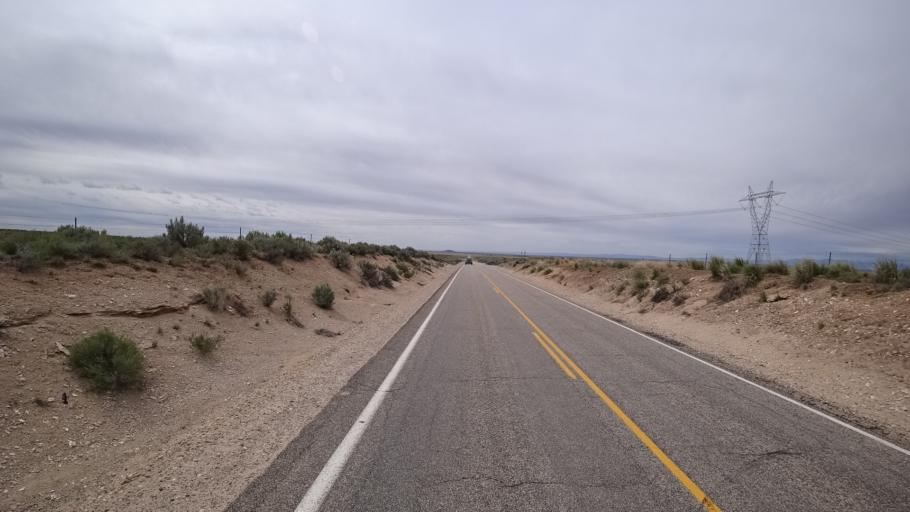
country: US
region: Idaho
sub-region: Ada County
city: Boise
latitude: 43.3727
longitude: -116.0049
